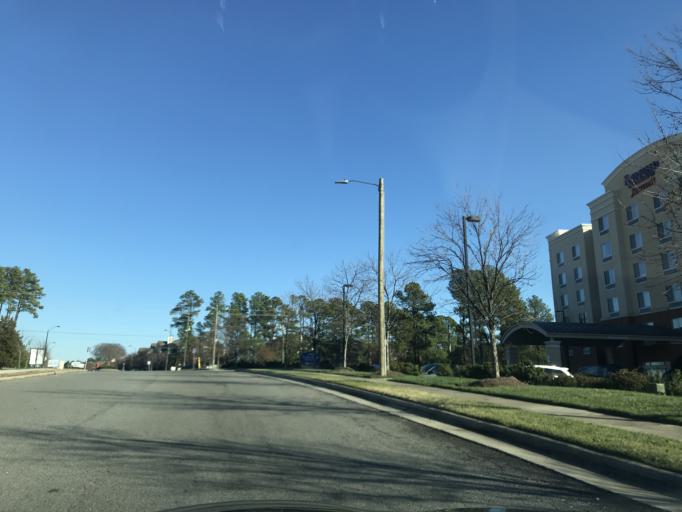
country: US
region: North Carolina
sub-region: Wake County
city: Morrisville
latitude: 35.8959
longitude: -78.8050
